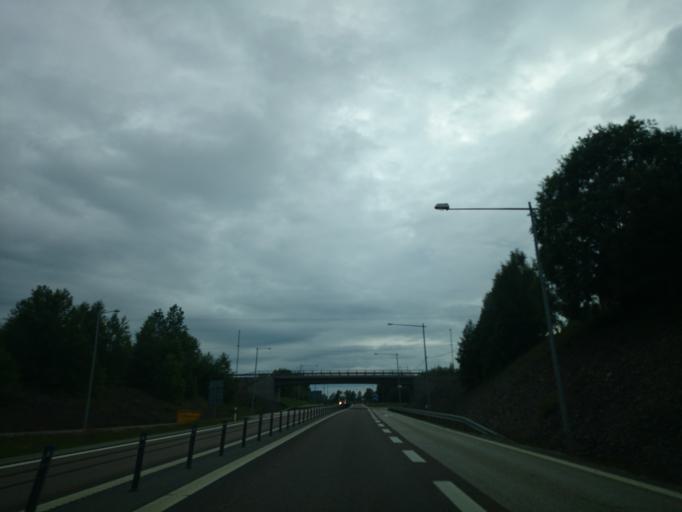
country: SE
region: Vaesternorrland
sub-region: Timra Kommun
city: Bergeforsen
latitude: 62.5164
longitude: 17.3941
